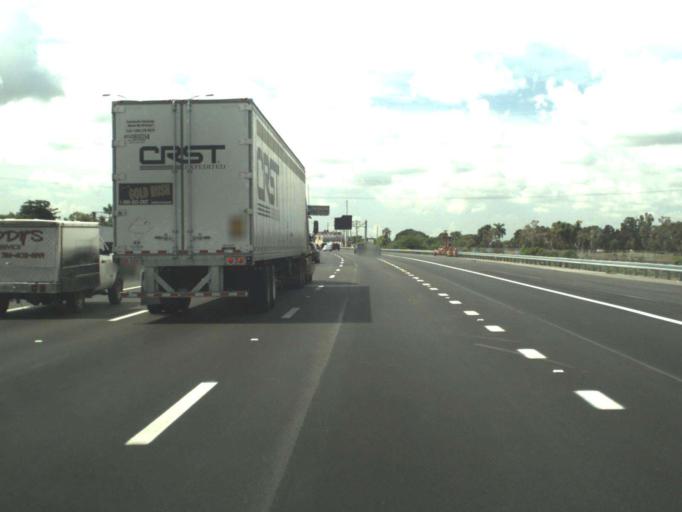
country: US
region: Florida
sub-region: Broward County
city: Pembroke Park
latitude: 26.0048
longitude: -80.1672
